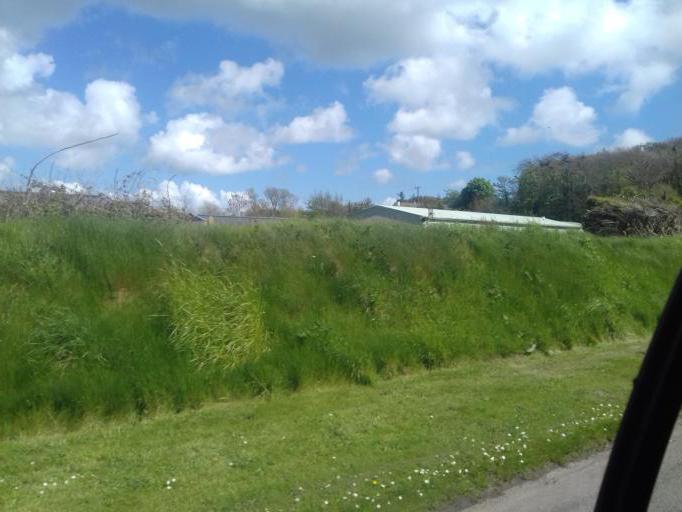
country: IE
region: Munster
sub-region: Waterford
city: Dunmore East
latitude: 52.2180
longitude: -6.9199
